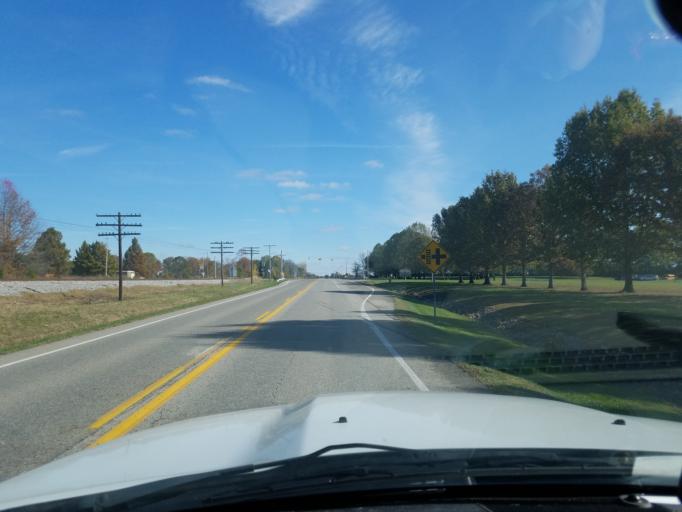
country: US
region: Indiana
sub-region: Jennings County
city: North Vernon
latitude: 39.0273
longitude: -85.5351
